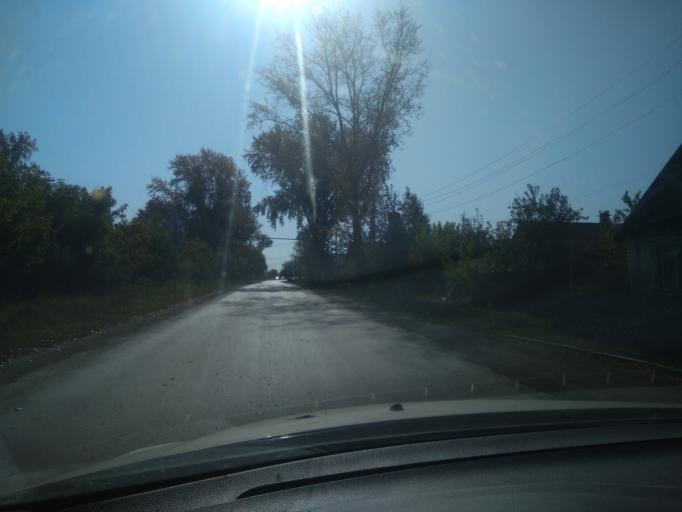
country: RU
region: Sverdlovsk
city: Pokrovskoye
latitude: 56.4653
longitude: 61.6151
